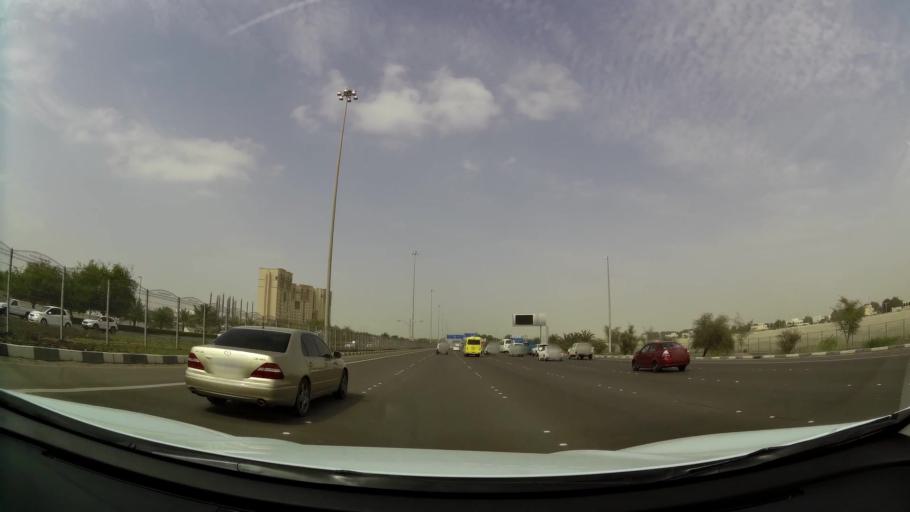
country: AE
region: Abu Dhabi
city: Abu Dhabi
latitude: 24.3800
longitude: 54.5248
